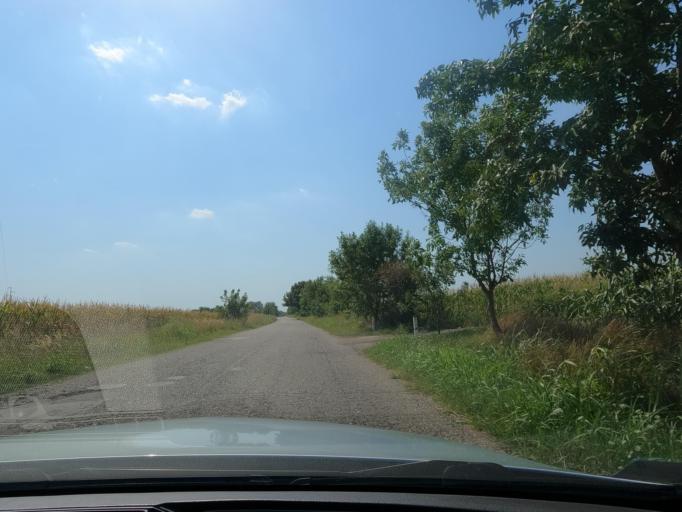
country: RS
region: Autonomna Pokrajina Vojvodina
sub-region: Severnobacki Okrug
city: Subotica
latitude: 46.0633
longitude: 19.7574
